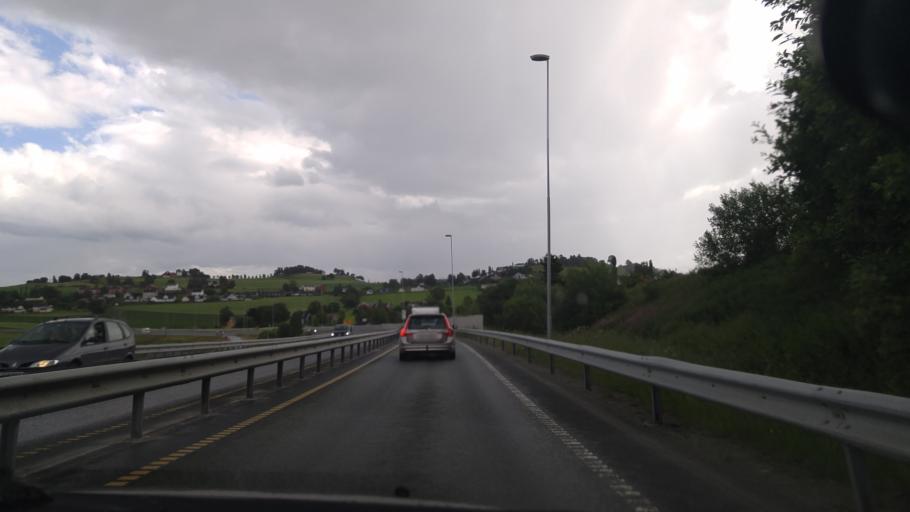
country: NO
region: Nord-Trondelag
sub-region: Levanger
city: Skogn
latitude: 63.7113
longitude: 11.1824
